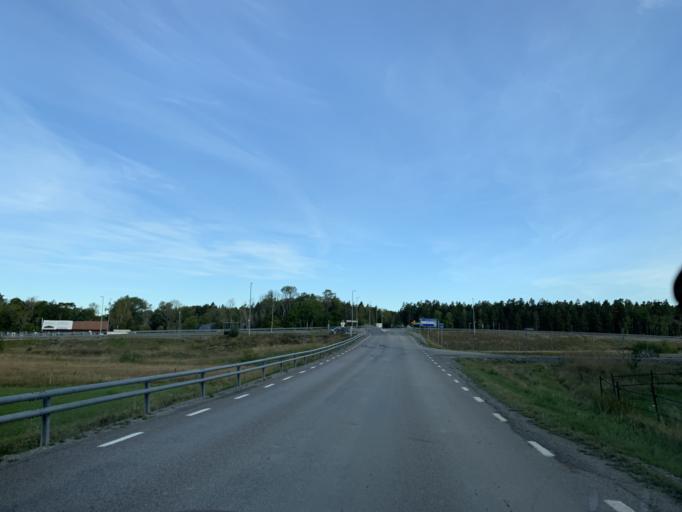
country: SE
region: Stockholm
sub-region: Haninge Kommun
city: Jordbro
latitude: 59.0665
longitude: 18.0650
